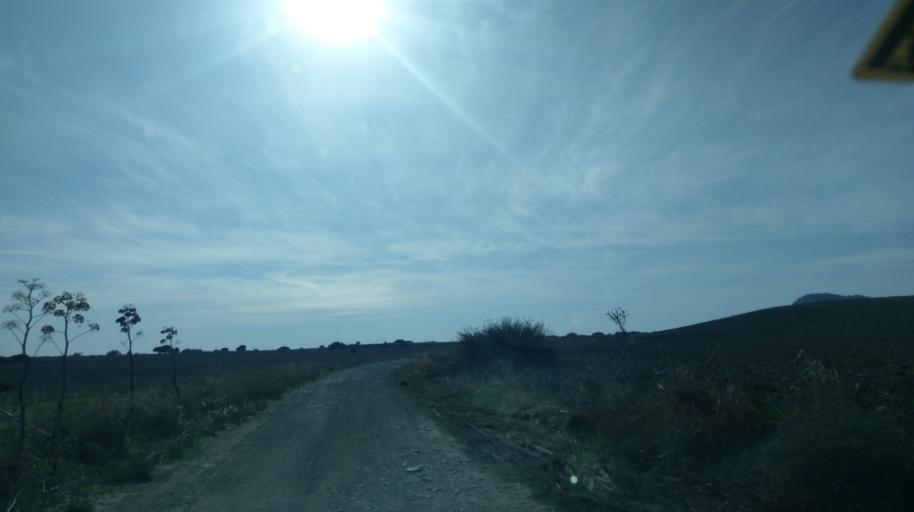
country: CY
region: Ammochostos
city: Trikomo
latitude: 35.3335
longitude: 33.8315
